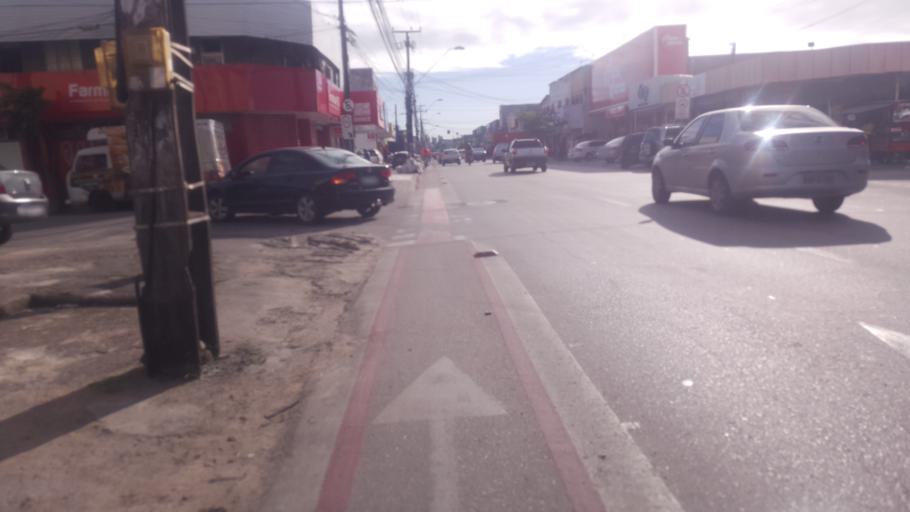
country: BR
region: Ceara
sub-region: Fortaleza
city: Fortaleza
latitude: -3.7638
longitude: -38.5479
